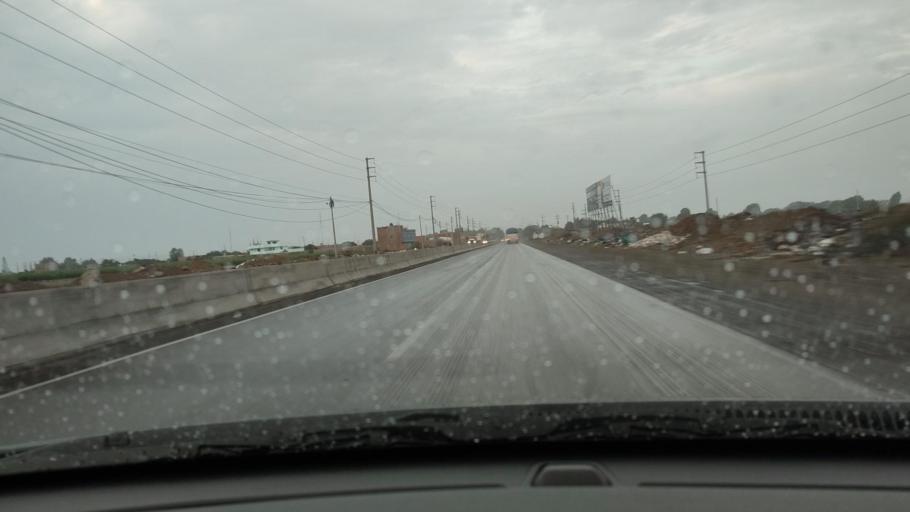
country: PE
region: La Libertad
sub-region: Provincia de Trujillo
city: Huanchaco
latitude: -8.0722
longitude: -79.0925
